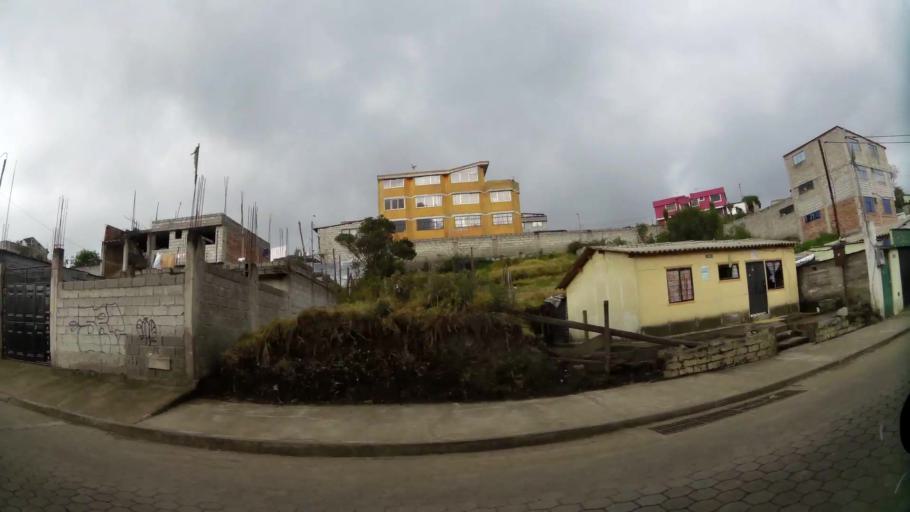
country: EC
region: Pichincha
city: Quito
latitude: -0.3023
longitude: -78.5226
